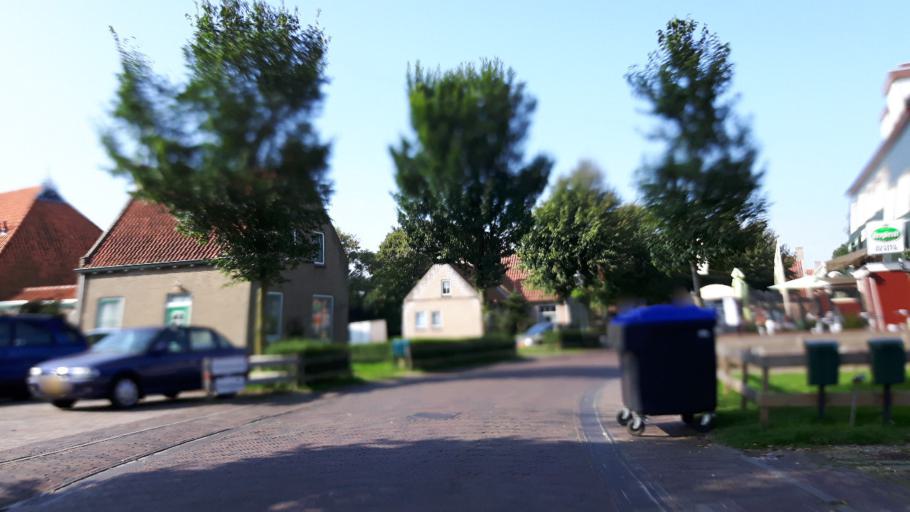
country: NL
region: Friesland
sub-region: Gemeente Ameland
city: Nes
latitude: 53.4474
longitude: 5.7992
